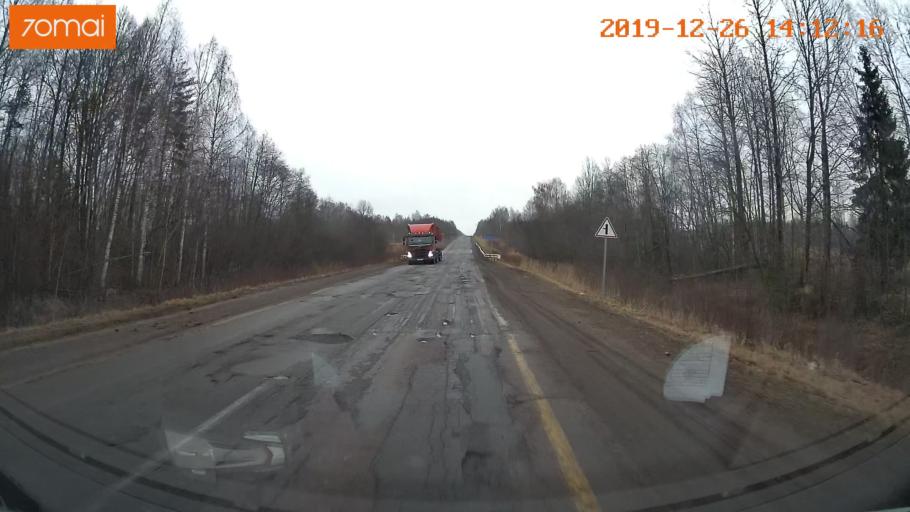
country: RU
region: Jaroslavl
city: Poshekhon'ye
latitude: 58.5108
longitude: 38.9876
